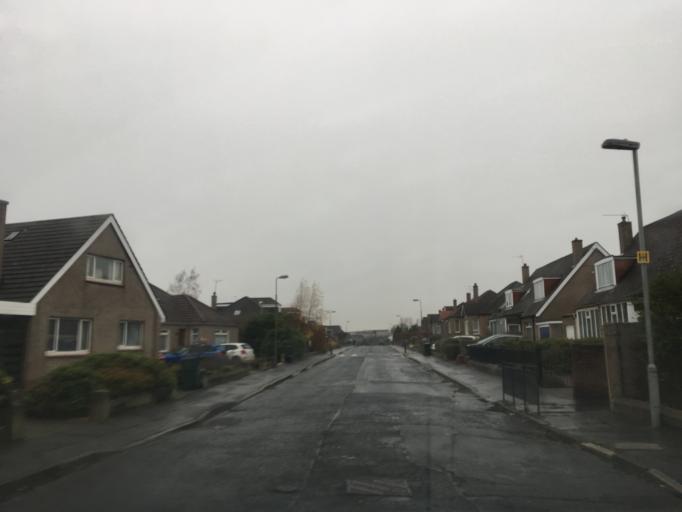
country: GB
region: Scotland
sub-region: Edinburgh
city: Currie
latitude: 55.9509
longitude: -3.2975
